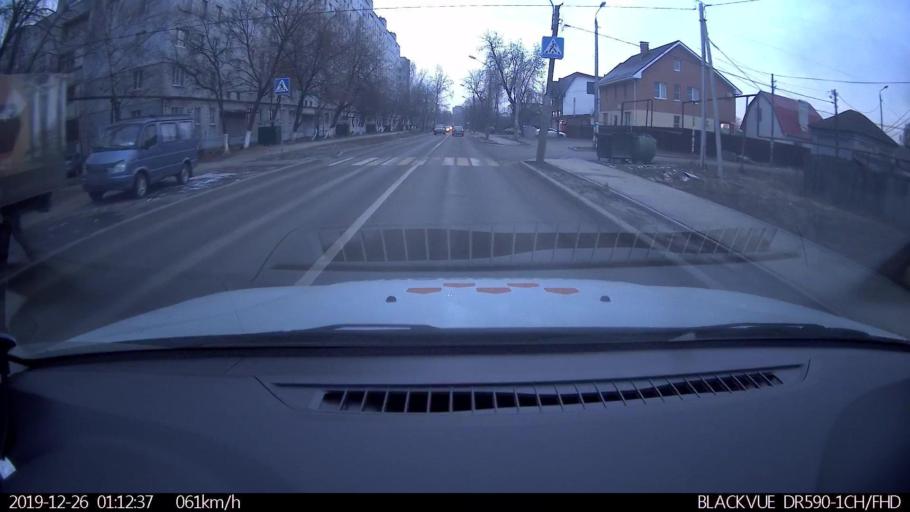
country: RU
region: Nizjnij Novgorod
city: Nizhniy Novgorod
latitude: 56.2833
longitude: 43.9151
